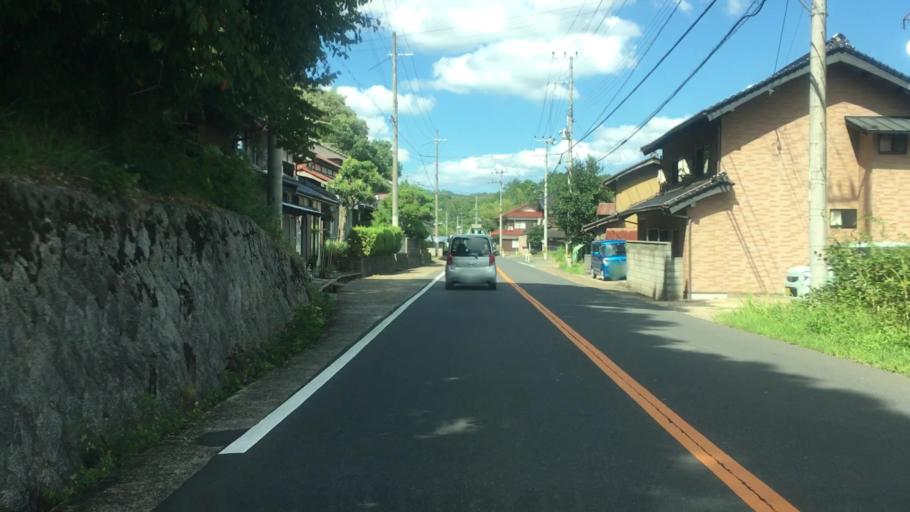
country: JP
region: Kyoto
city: Miyazu
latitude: 35.6114
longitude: 135.0537
